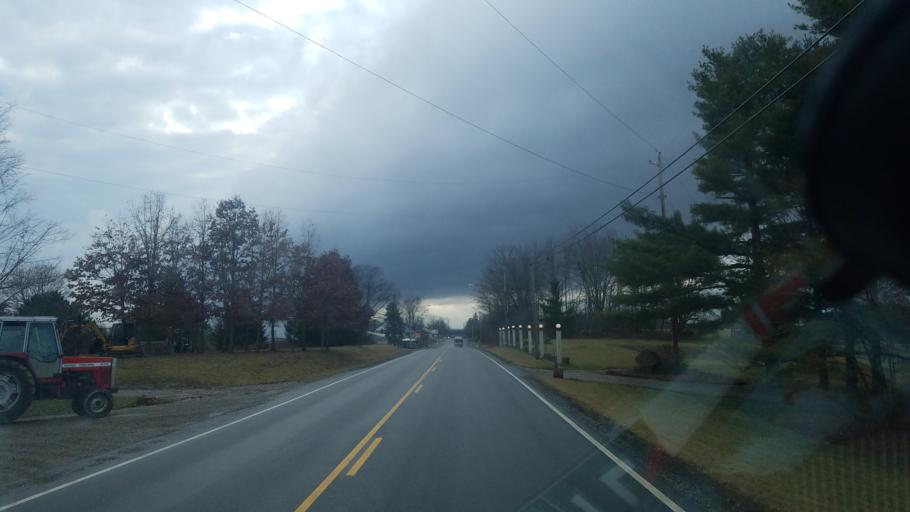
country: US
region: Ohio
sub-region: Knox County
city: Oak Hill
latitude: 40.3372
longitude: -82.1602
